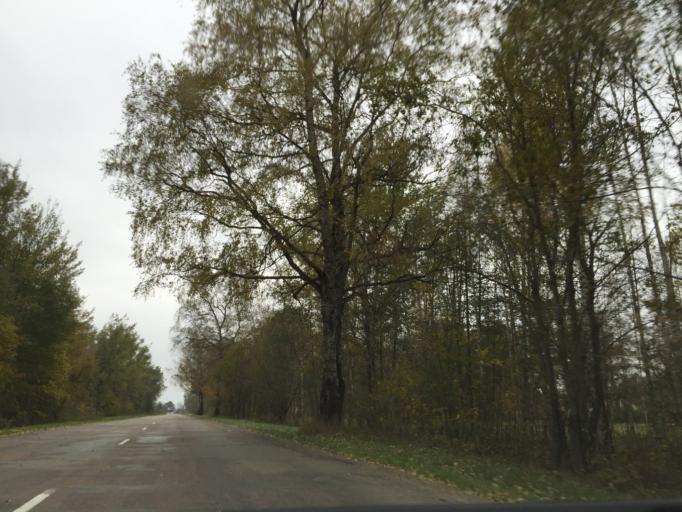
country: LV
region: Marupe
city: Marupe
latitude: 56.8512
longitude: 24.0523
